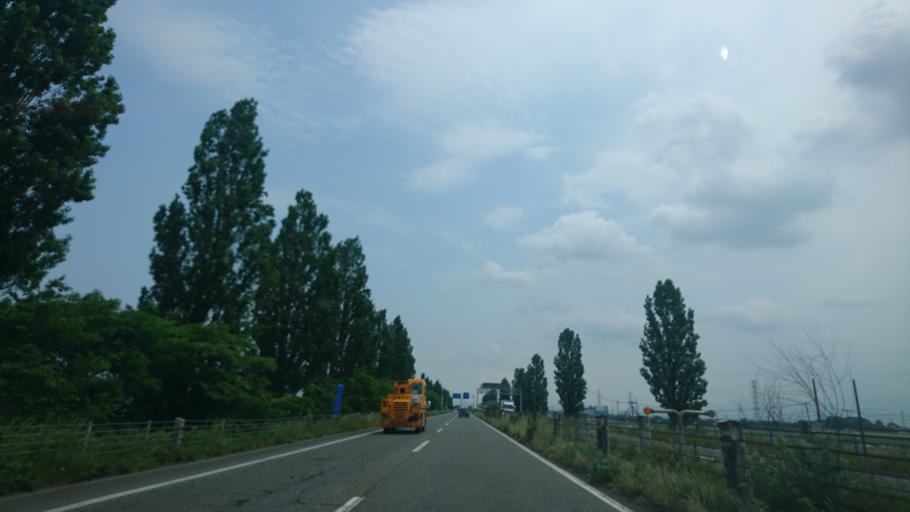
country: JP
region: Niigata
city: Kameda-honcho
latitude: 37.9380
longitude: 139.1736
